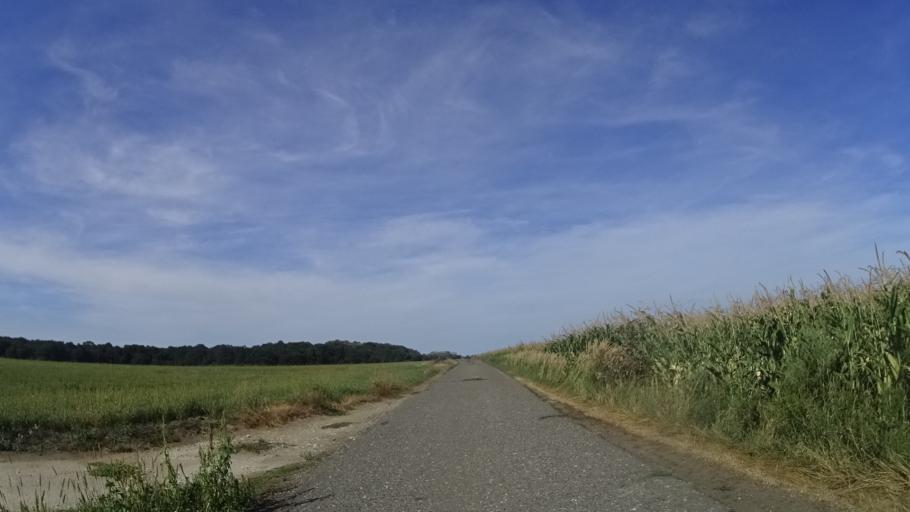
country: AT
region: Lower Austria
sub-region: Politischer Bezirk Ganserndorf
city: Durnkrut
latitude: 48.4528
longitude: 16.8876
